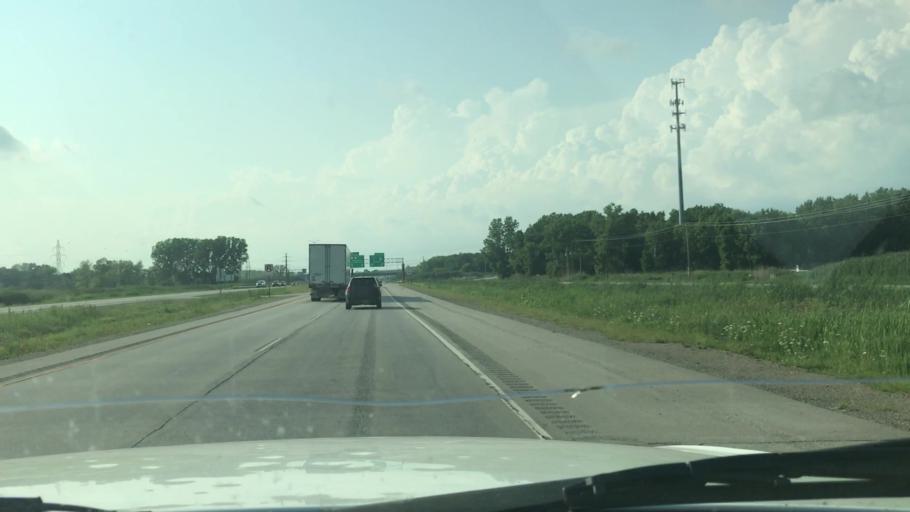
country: US
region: Wisconsin
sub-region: Brown County
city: Green Bay
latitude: 44.5485
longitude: -88.0368
